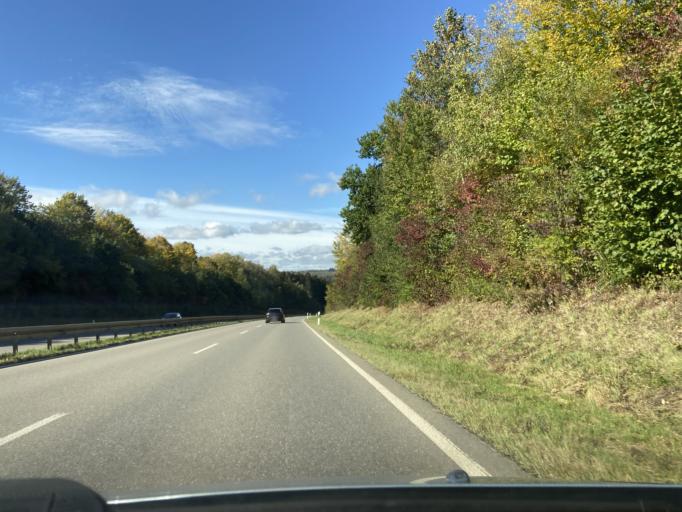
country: DE
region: Baden-Wuerttemberg
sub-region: Tuebingen Region
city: Sigmaringen
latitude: 48.0715
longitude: 9.2146
